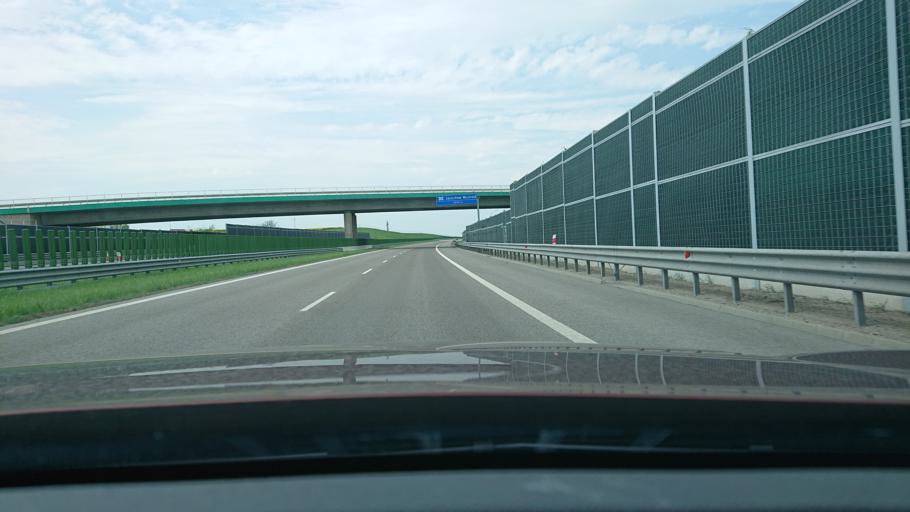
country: PL
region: Subcarpathian Voivodeship
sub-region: Powiat jaroslawski
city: Rokietnica
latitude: 49.9439
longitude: 22.6692
